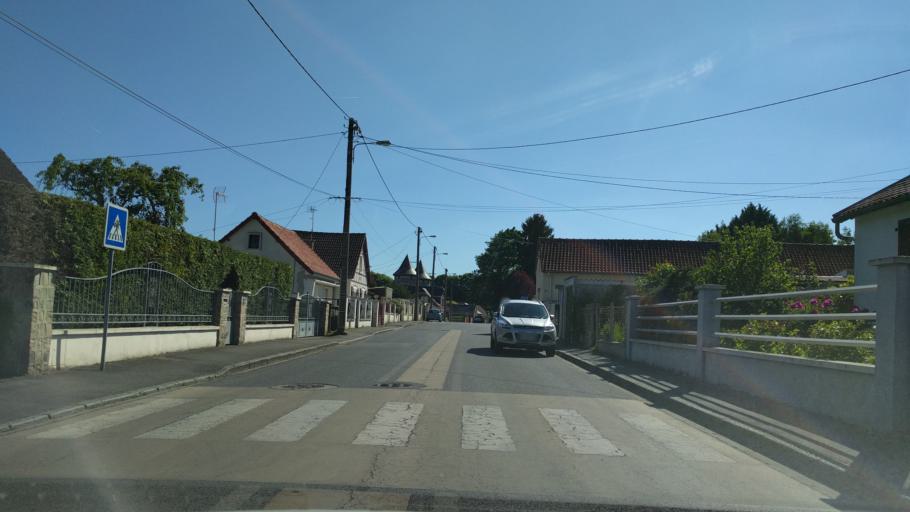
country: FR
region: Picardie
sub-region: Departement de la Somme
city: Peronne
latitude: 49.9303
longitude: 2.9278
